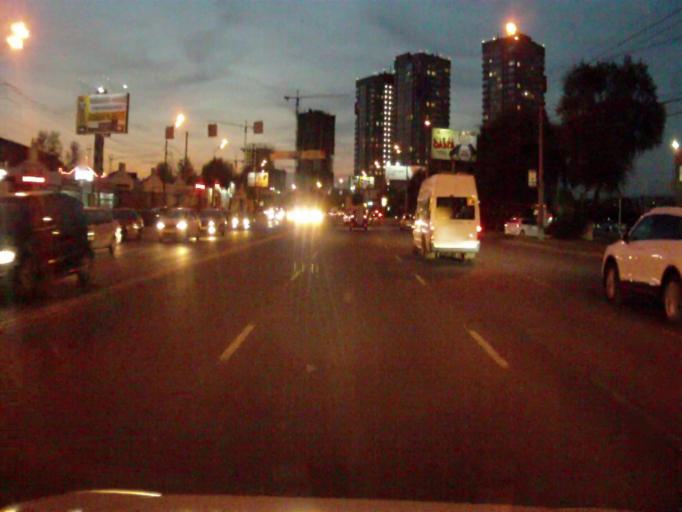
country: RU
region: Chelyabinsk
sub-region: Gorod Chelyabinsk
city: Chelyabinsk
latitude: 55.1698
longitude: 61.3742
